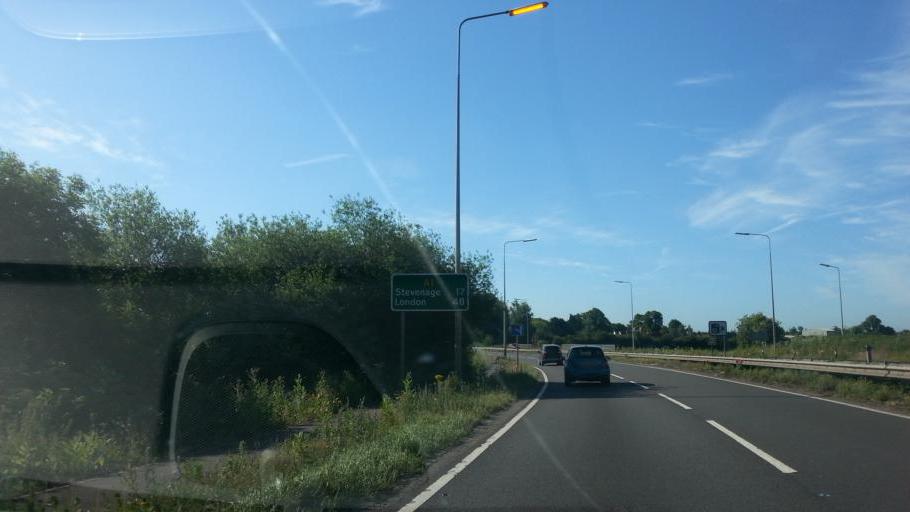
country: GB
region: England
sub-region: Central Bedfordshire
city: Sandy
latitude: 52.1241
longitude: -0.2980
